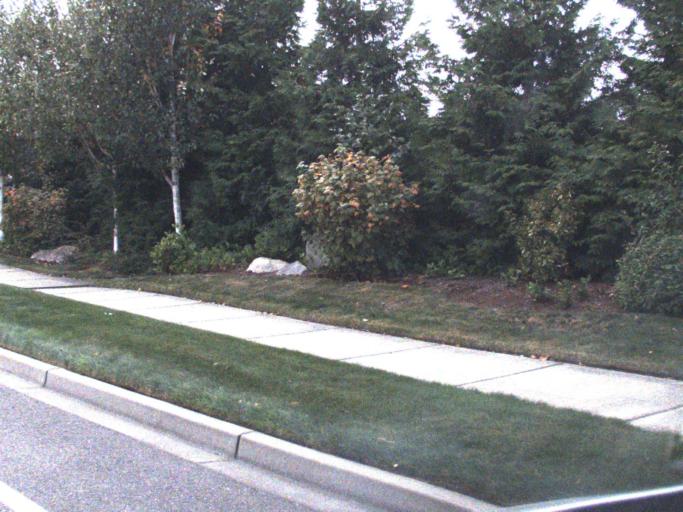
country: US
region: Washington
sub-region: Jefferson County
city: Port Hadlock-Irondale
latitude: 48.0576
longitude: -122.8192
